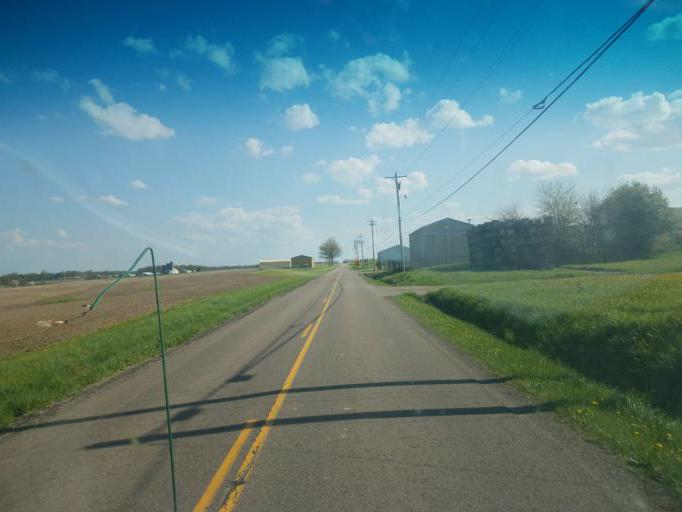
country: US
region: Ohio
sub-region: Wayne County
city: Smithville
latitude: 40.8790
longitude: -81.8782
